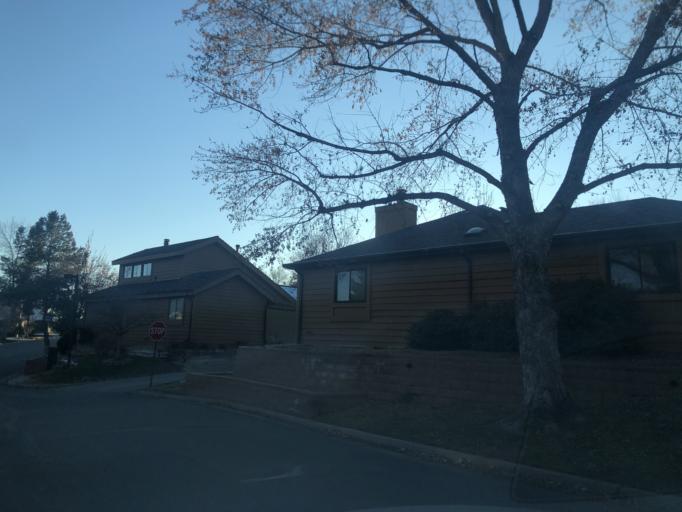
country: US
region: Colorado
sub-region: Adams County
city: Aurora
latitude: 39.7154
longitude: -104.8153
